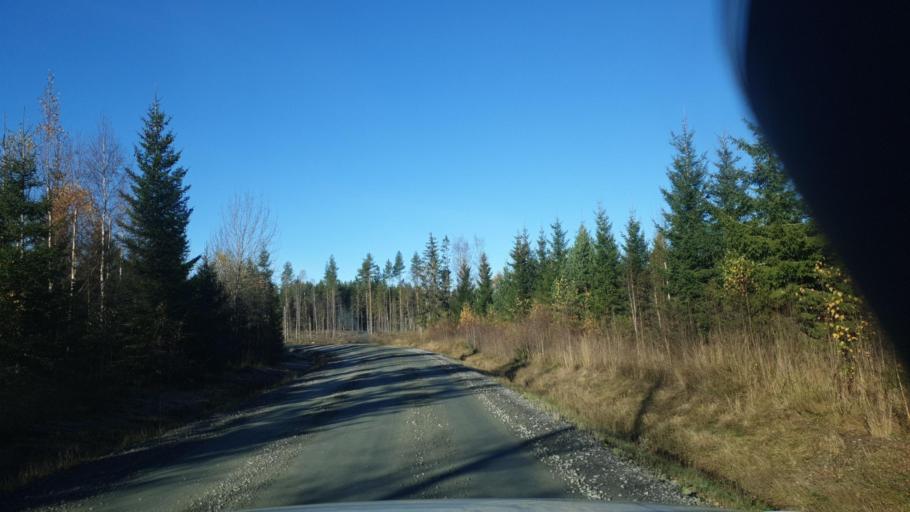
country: SE
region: Vaermland
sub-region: Karlstads Kommun
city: Edsvalla
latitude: 59.4463
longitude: 13.1639
